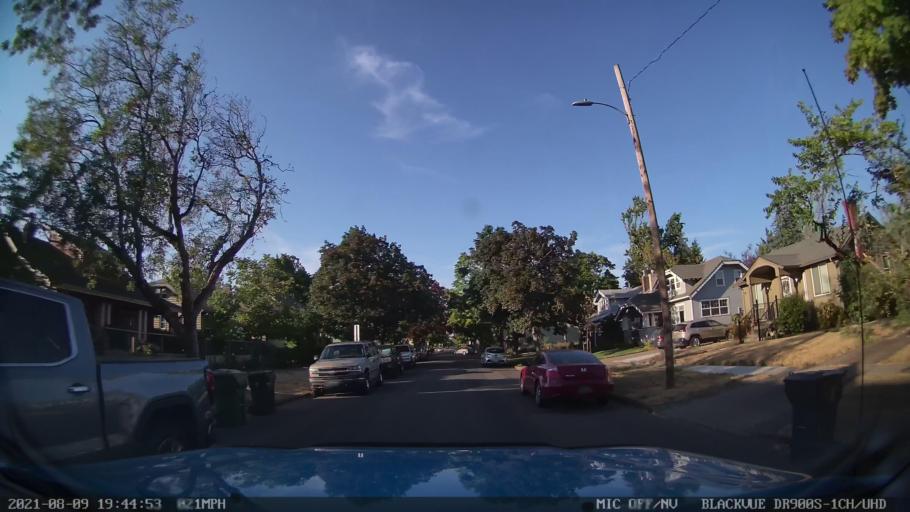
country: US
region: Oregon
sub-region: Marion County
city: Salem
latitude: 44.9493
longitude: -123.0309
